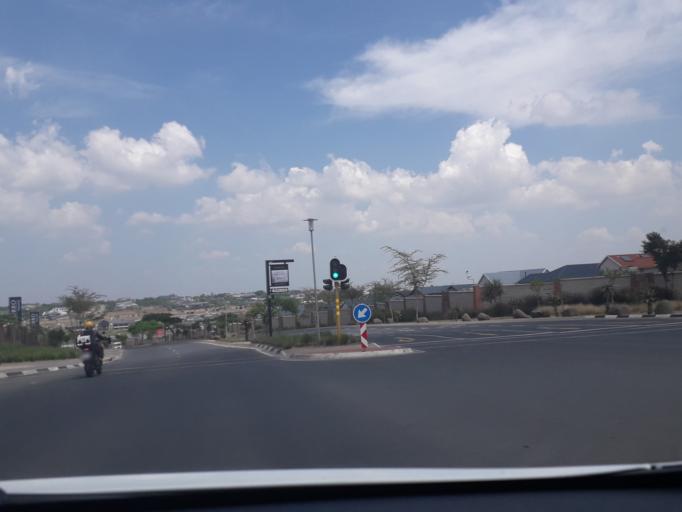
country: ZA
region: Gauteng
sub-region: City of Johannesburg Metropolitan Municipality
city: Midrand
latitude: -26.0142
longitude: 28.0961
